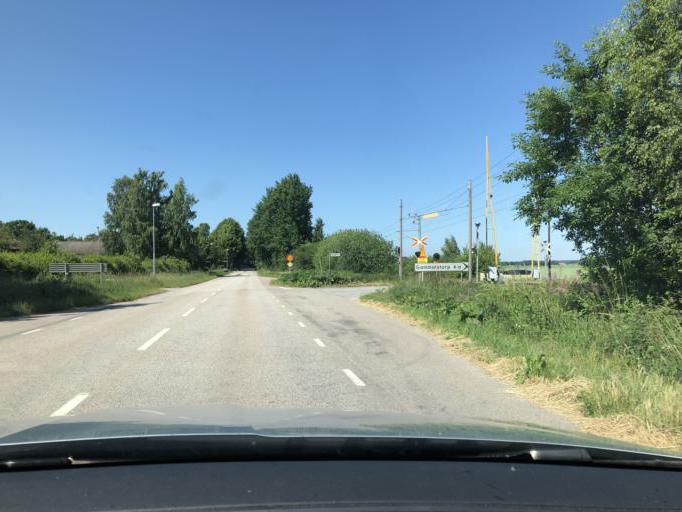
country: SE
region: Blekinge
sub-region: Solvesborgs Kommun
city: Soelvesborg
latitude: 56.1068
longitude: 14.6197
